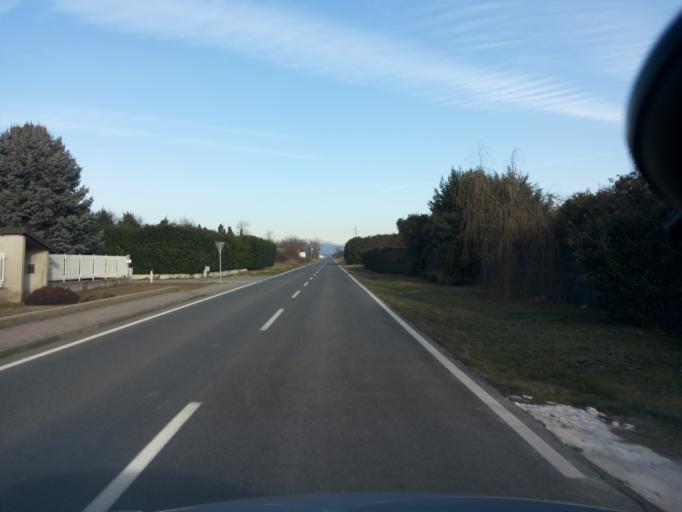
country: IT
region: Piedmont
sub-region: Provincia di Vercelli
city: Ghislarengo
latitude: 45.5375
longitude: 8.3855
